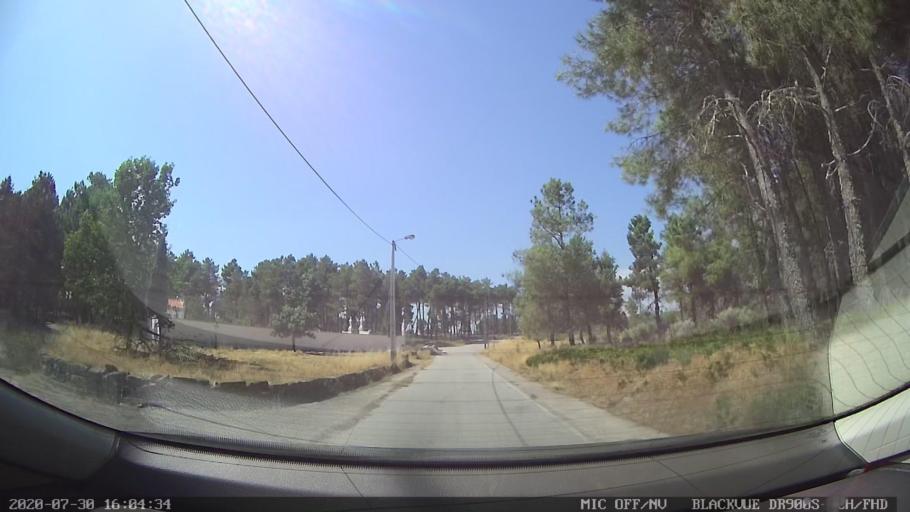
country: PT
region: Vila Real
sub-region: Murca
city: Murca
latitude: 41.3507
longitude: -7.4858
